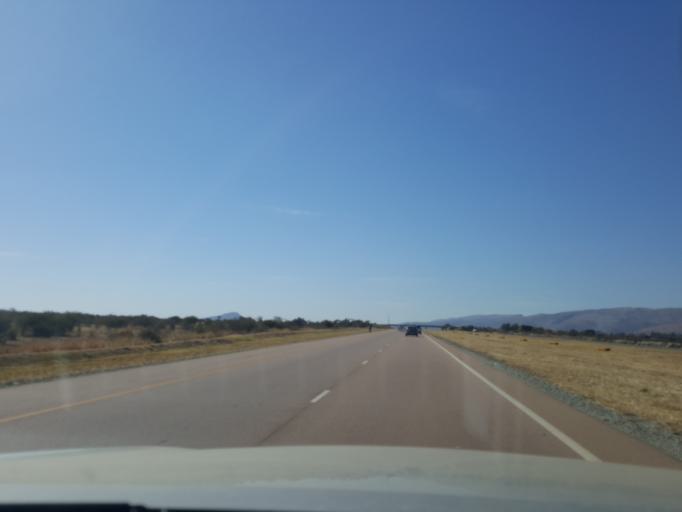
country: ZA
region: North-West
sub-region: Bojanala Platinum District Municipality
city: Brits
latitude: -25.7369
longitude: 27.6250
